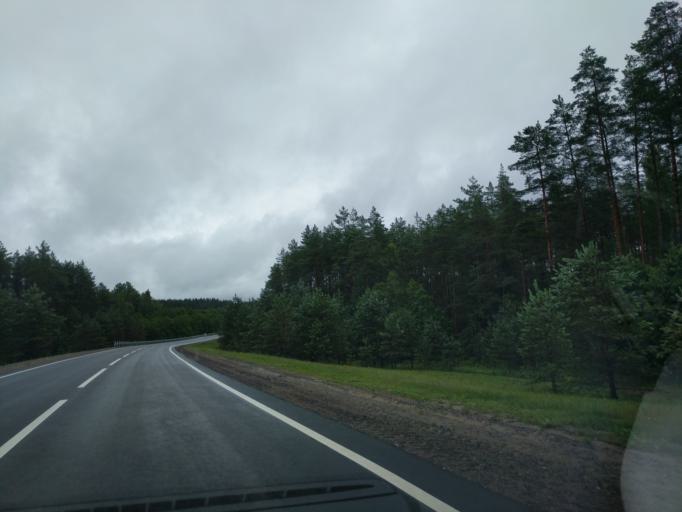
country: BY
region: Minsk
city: Syomkava
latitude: 54.2047
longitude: 27.4947
